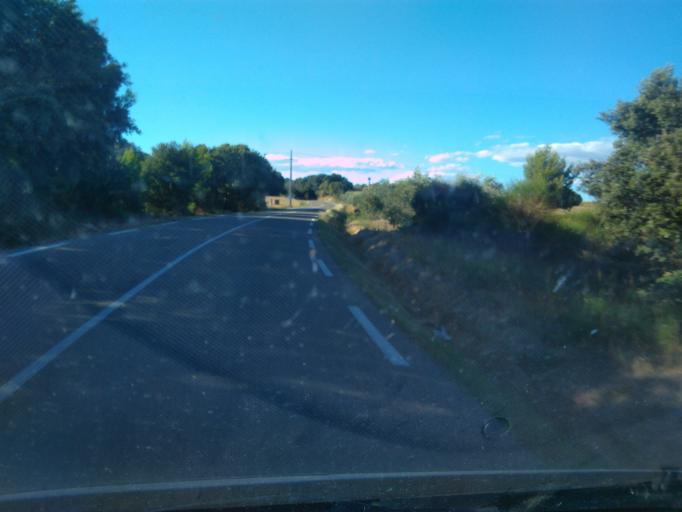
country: FR
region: Languedoc-Roussillon
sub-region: Departement du Gard
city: Vauvert
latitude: 43.6685
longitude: 4.2827
